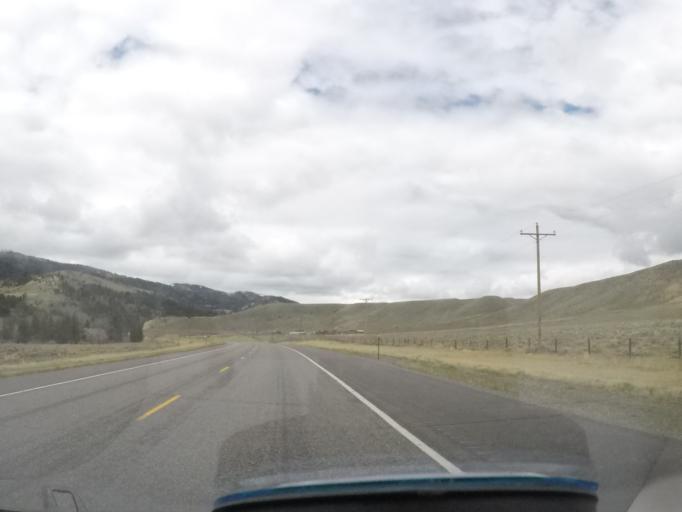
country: US
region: Wyoming
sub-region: Sublette County
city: Pinedale
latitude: 43.5788
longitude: -109.7441
